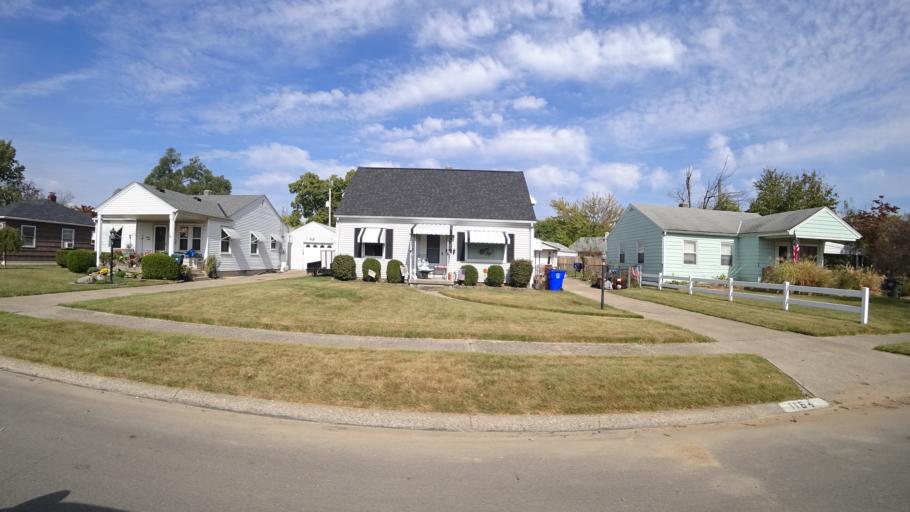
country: US
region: Ohio
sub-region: Butler County
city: Fairfield
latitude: 39.3595
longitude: -84.5451
